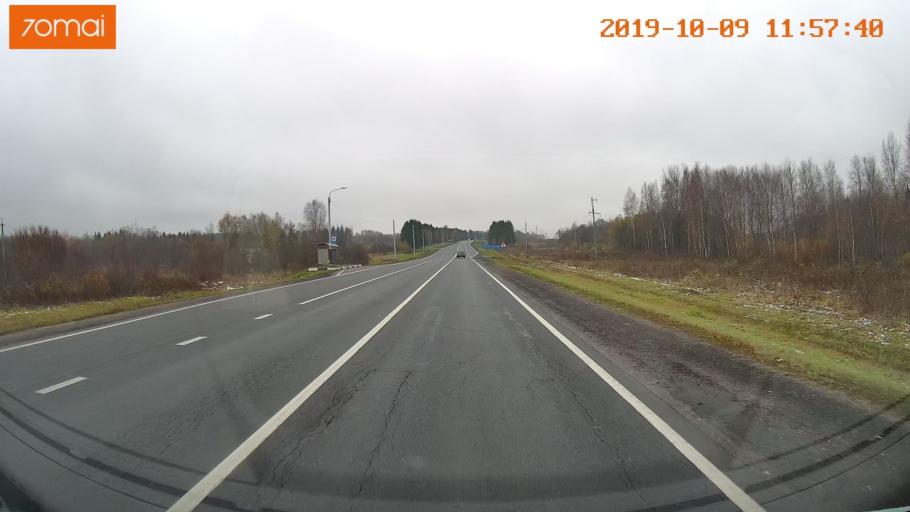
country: RU
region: Vologda
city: Gryazovets
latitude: 58.7292
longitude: 40.2939
